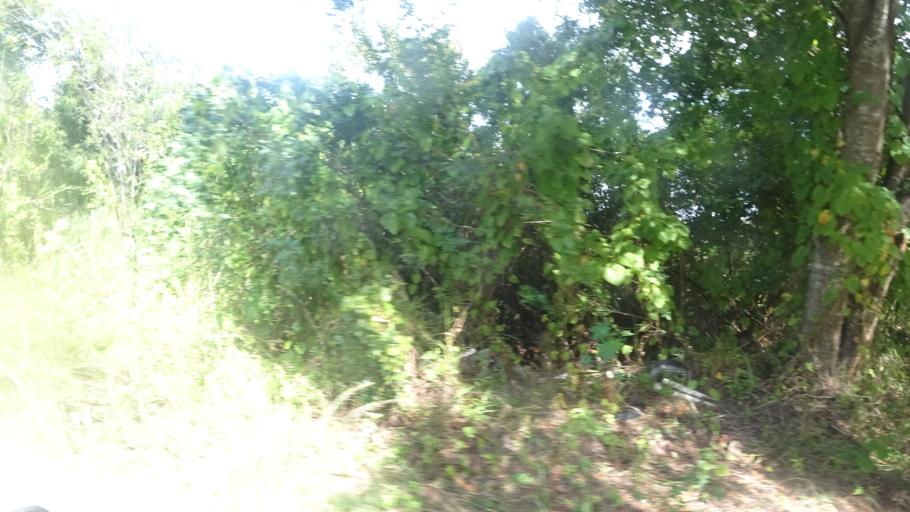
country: US
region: Florida
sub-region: Hillsborough County
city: Sun City Center
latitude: 27.6438
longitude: -82.3621
